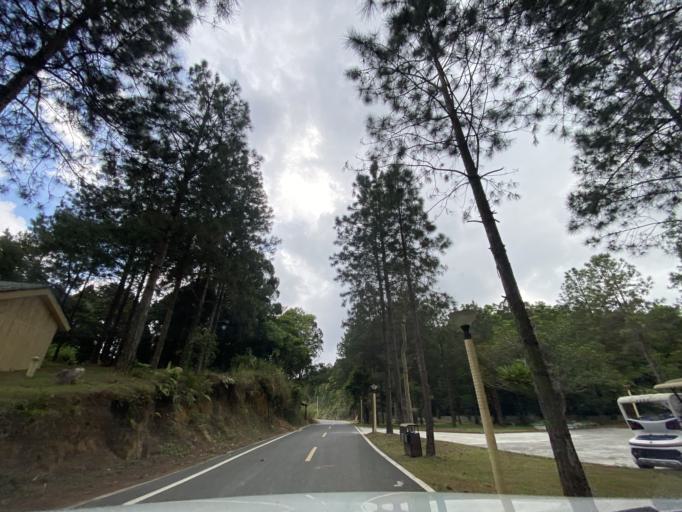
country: CN
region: Hainan
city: Diaoluoshan
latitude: 18.7248
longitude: 109.8686
